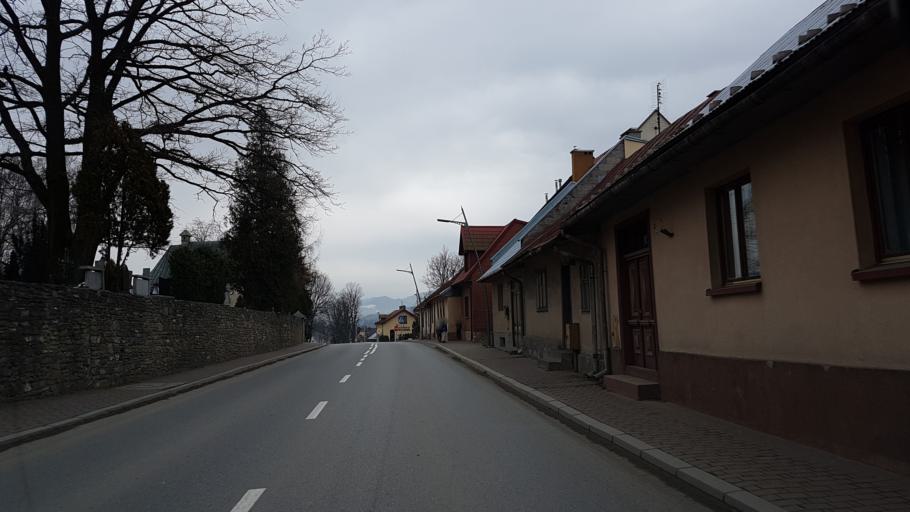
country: PL
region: Lesser Poland Voivodeship
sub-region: Powiat nowosadecki
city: Stary Sacz
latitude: 49.5578
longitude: 20.6376
